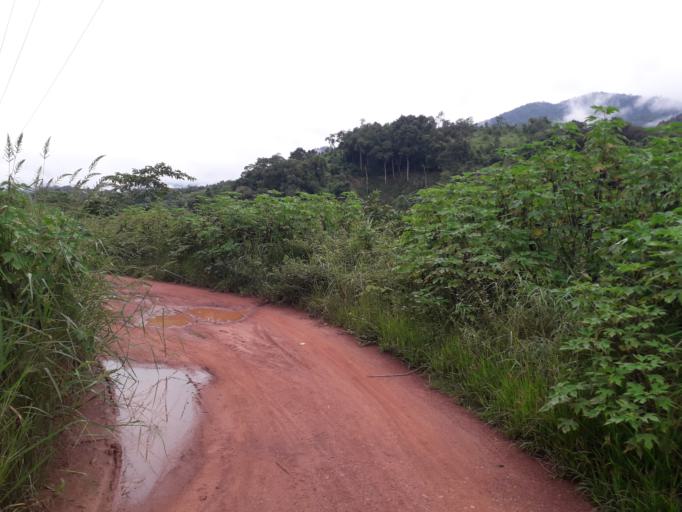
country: CN
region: Yunnan
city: Menglie
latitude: 22.2441
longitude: 101.6089
